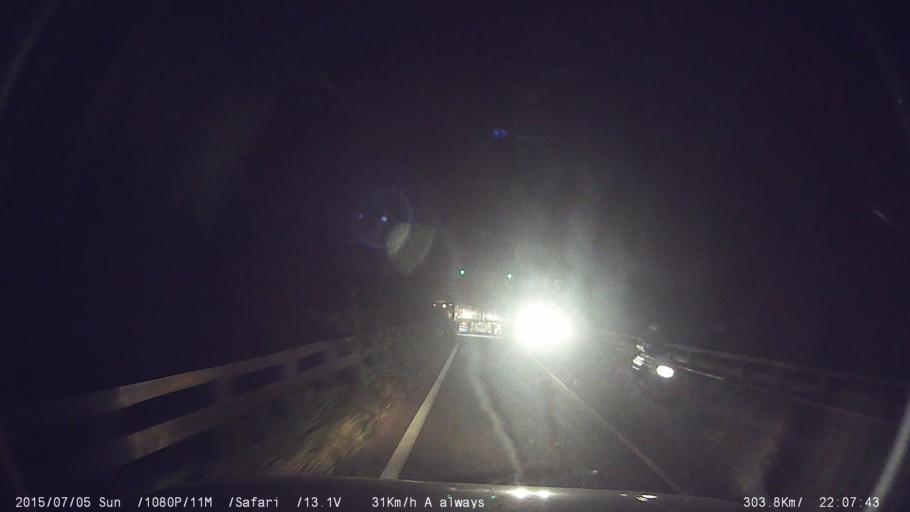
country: IN
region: Kerala
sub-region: Palakkad district
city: Mannarakkat
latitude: 10.9057
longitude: 76.5311
